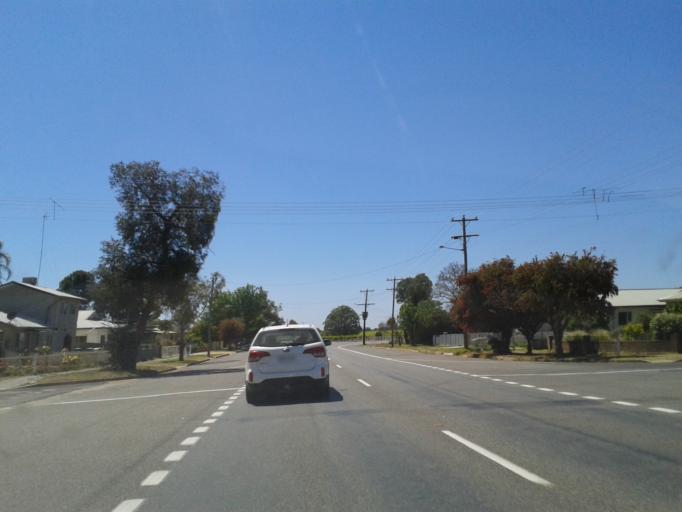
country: AU
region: New South Wales
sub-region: Wentworth
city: Dareton
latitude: -34.0943
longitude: 142.0455
